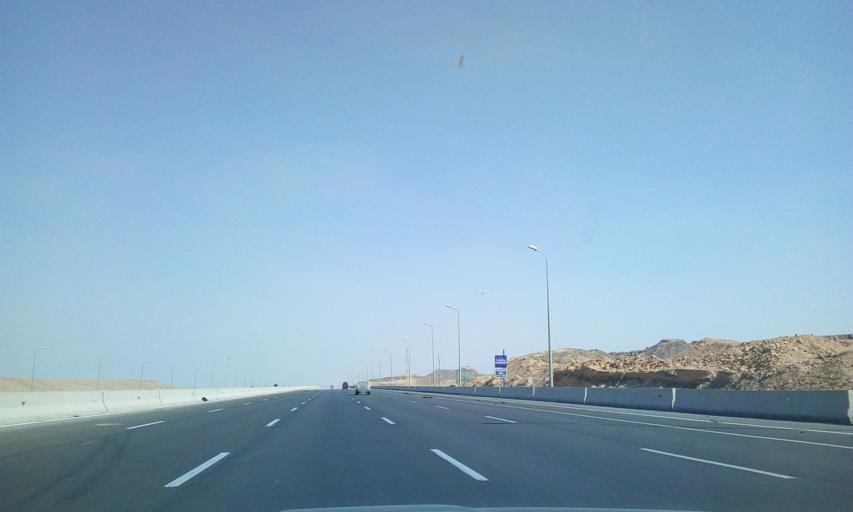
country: EG
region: As Suways
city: Ain Sukhna
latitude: 29.7055
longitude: 32.0885
